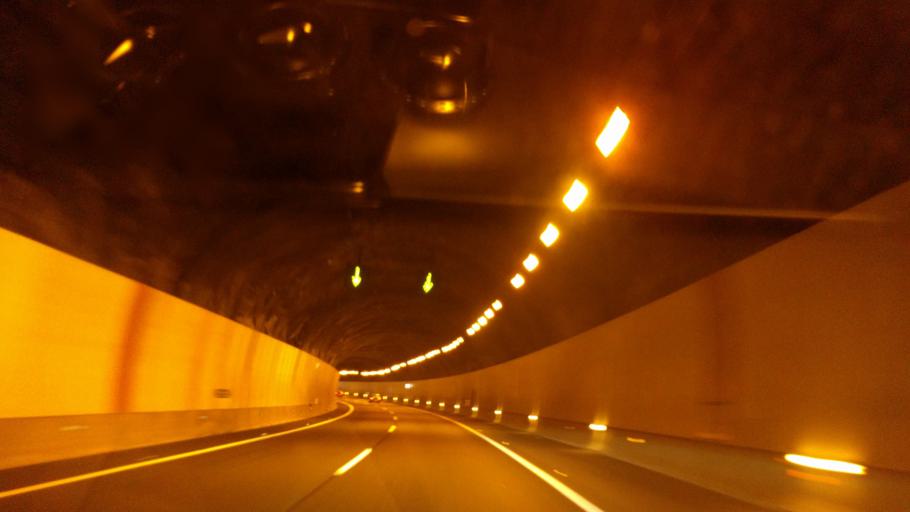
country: ES
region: Cantabria
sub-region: Provincia de Cantabria
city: Liendo
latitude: 43.4026
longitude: -3.3098
